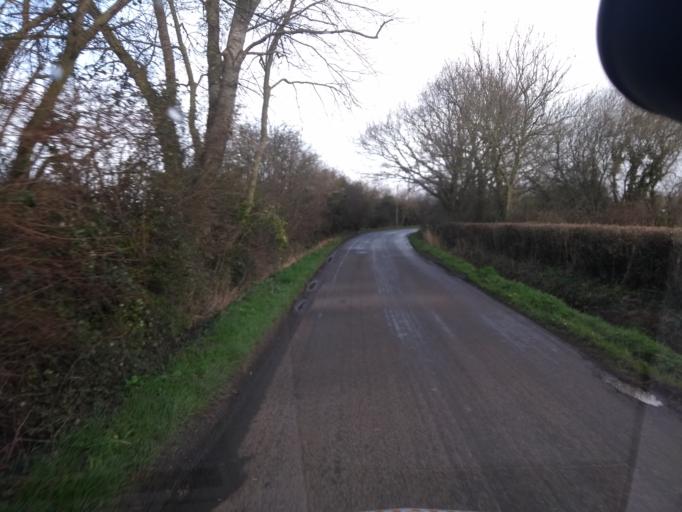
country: GB
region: England
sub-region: Somerset
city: South Petherton
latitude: 50.9724
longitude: -2.7974
